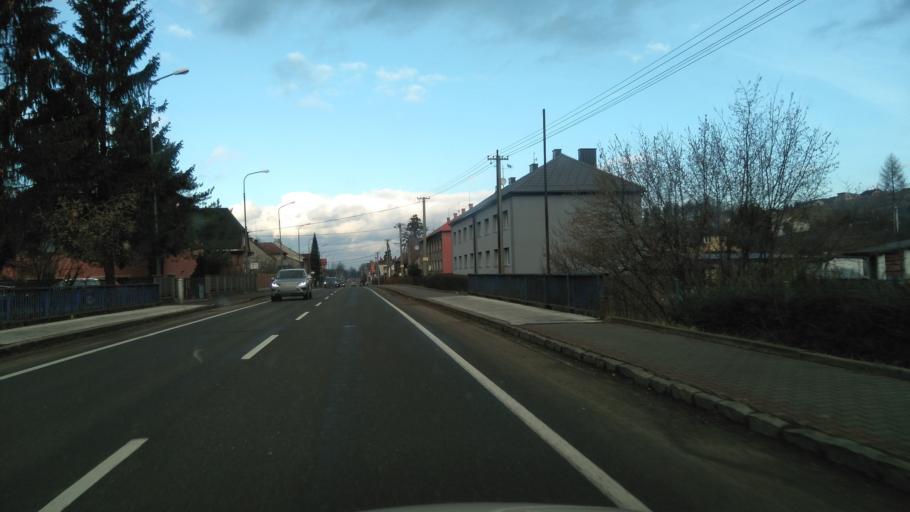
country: CZ
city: Navsi u Jablunkova
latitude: 49.5843
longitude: 18.7617
